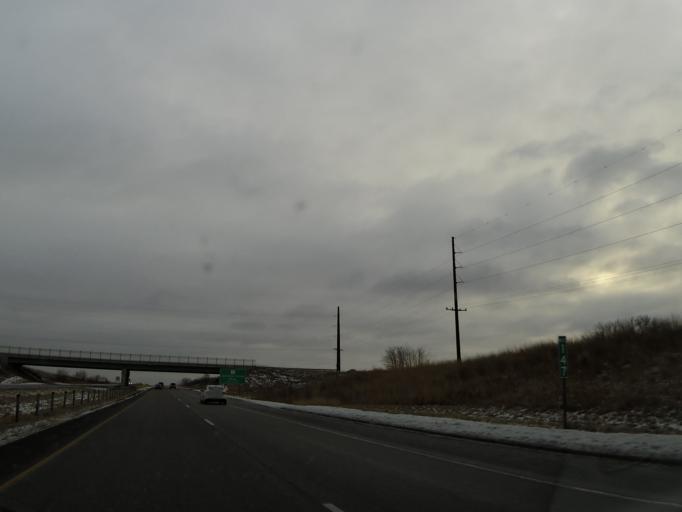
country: US
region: Minnesota
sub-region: Carver County
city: Carver
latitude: 44.7925
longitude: -93.6320
